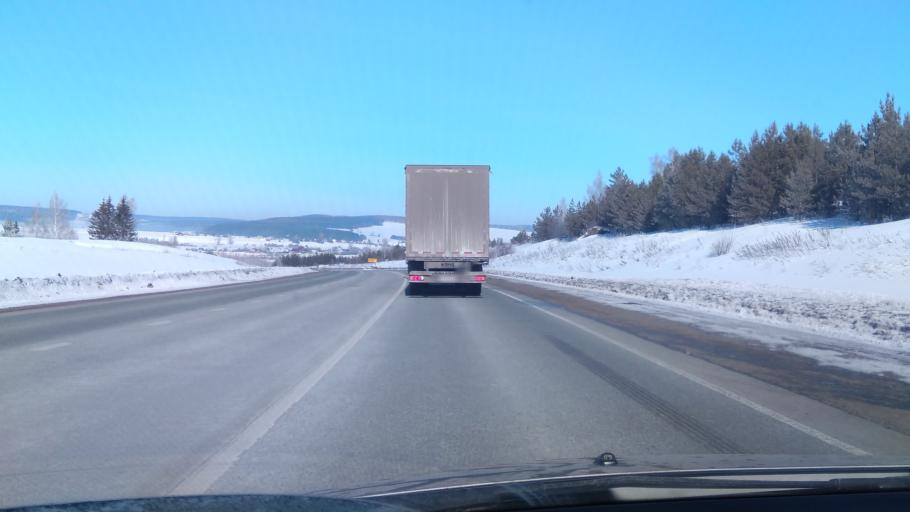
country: RU
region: Perm
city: Suksun
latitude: 57.0429
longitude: 57.4404
